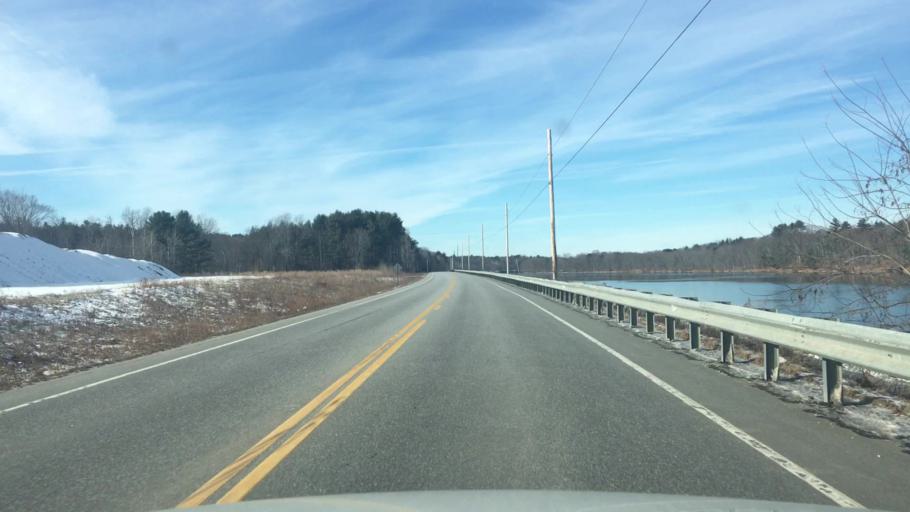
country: US
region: Maine
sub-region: Androscoggin County
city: Lisbon
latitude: 43.9988
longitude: -70.1487
